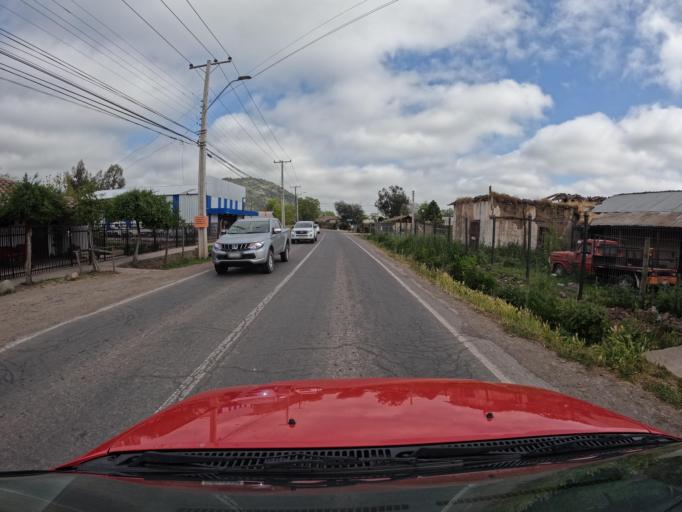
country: CL
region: O'Higgins
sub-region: Provincia de Colchagua
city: Santa Cruz
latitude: -34.7085
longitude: -71.2956
